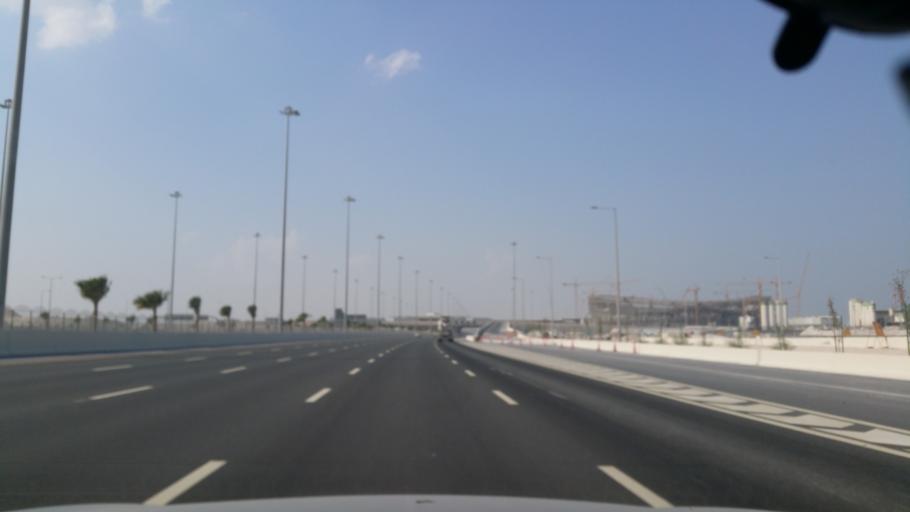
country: QA
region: Baladiyat Umm Salal
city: Umm Salal Muhammad
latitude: 25.4079
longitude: 51.4900
